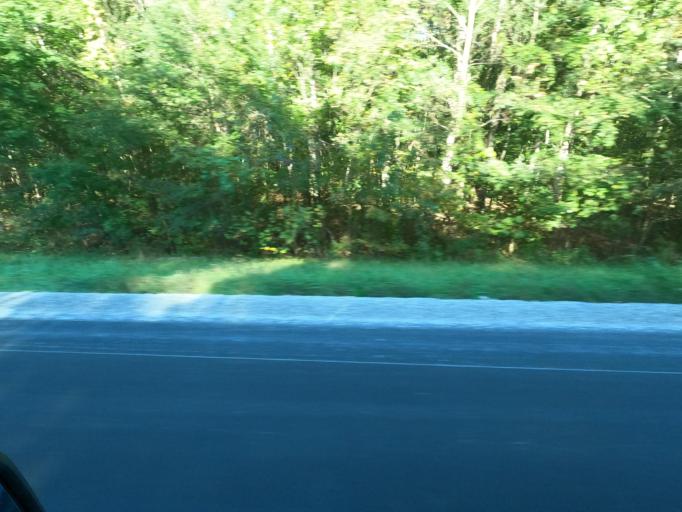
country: US
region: Tennessee
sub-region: Coffee County
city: Manchester
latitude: 35.4430
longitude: -86.0418
